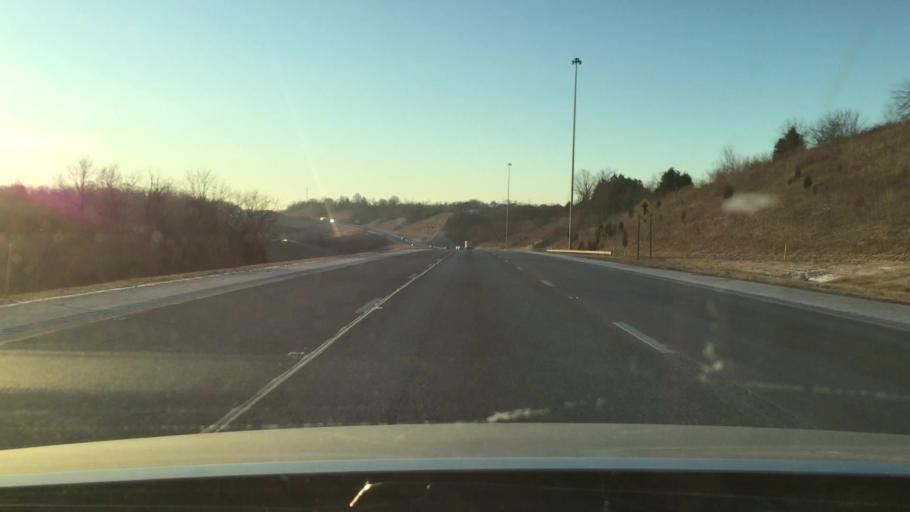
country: US
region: Kentucky
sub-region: Grant County
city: Williamstown
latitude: 38.6441
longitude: -84.5864
